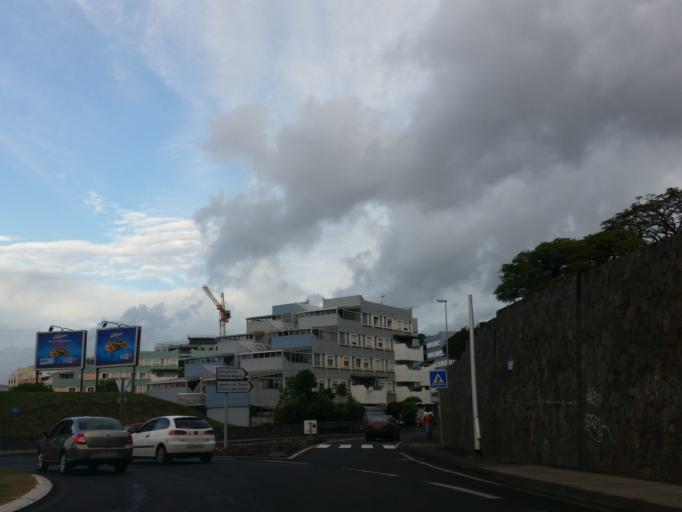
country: RE
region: Reunion
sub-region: Reunion
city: Saint-Denis
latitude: -20.9010
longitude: 55.4872
